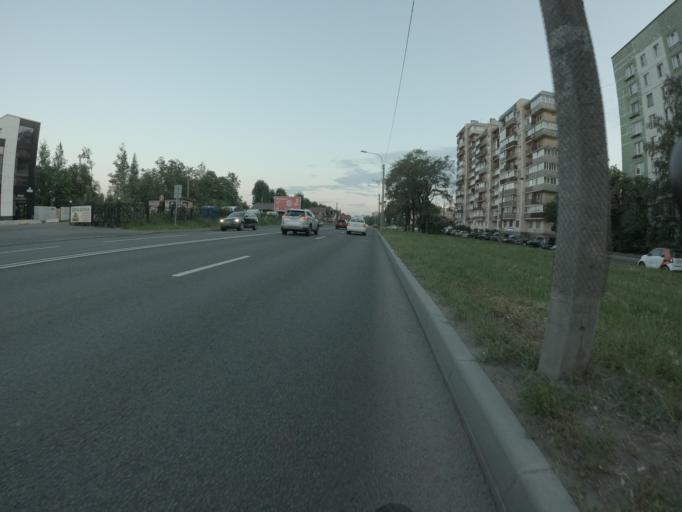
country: RU
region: St.-Petersburg
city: Dachnoye
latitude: 59.8447
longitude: 30.2788
